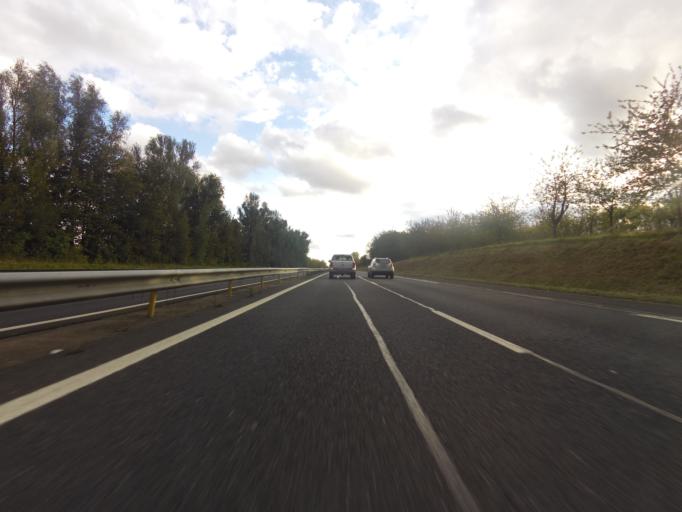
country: FR
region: Haute-Normandie
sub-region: Departement de la Seine-Maritime
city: Saint-Martin-Osmonville
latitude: 49.5776
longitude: 1.2755
